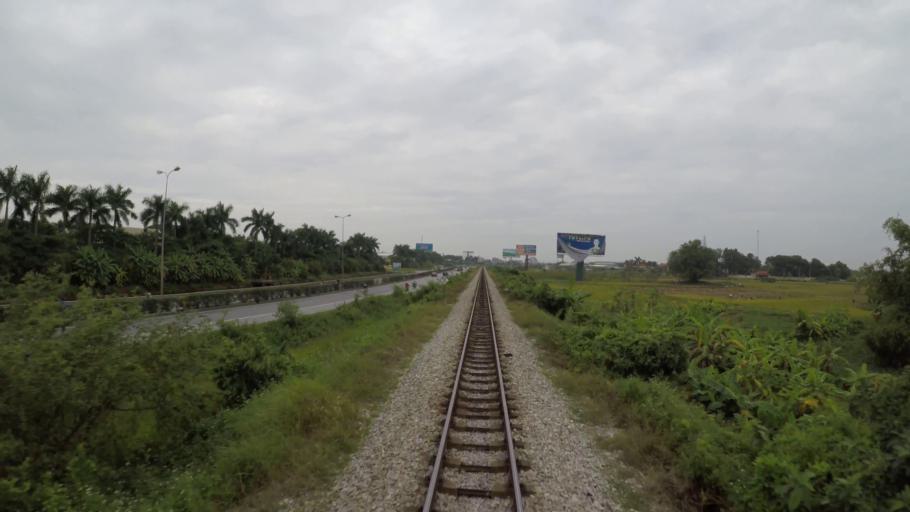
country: VN
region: Hai Duong
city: Thanh Pho Hai Duong
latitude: 20.9609
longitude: 106.3709
